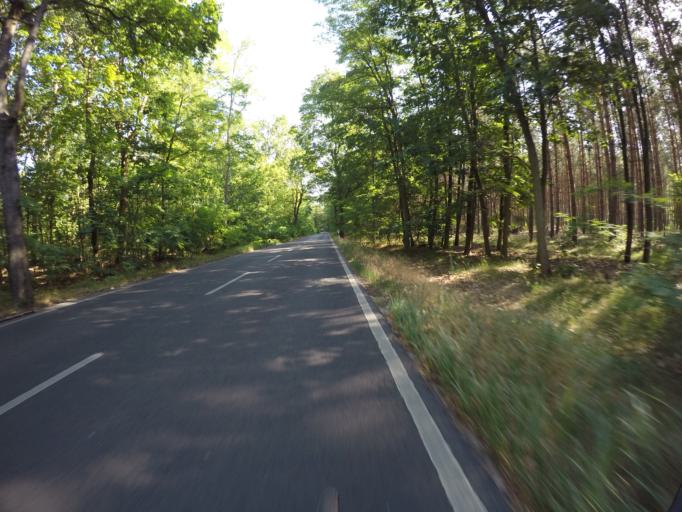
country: DE
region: Berlin
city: Schmockwitz
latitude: 52.3713
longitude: 13.6578
